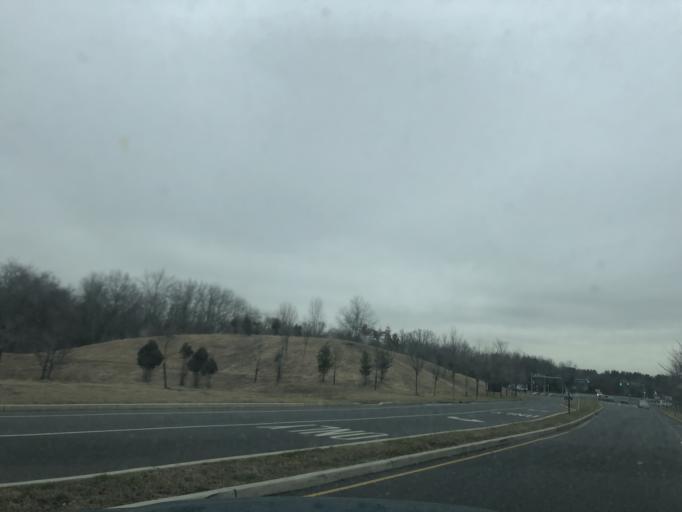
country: US
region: New Jersey
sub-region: Middlesex County
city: Plainsboro Center
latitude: 40.3435
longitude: -74.6158
